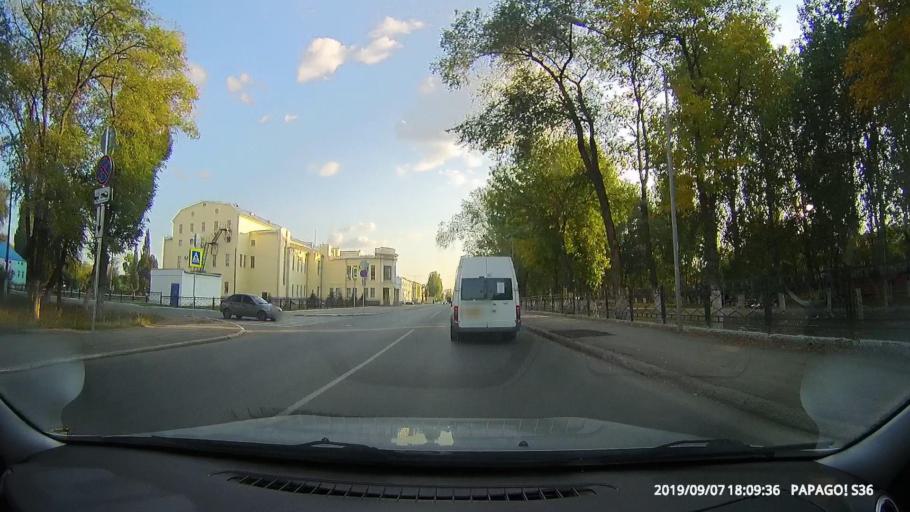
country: RU
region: Samara
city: Chapayevsk
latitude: 52.9972
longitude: 49.7701
